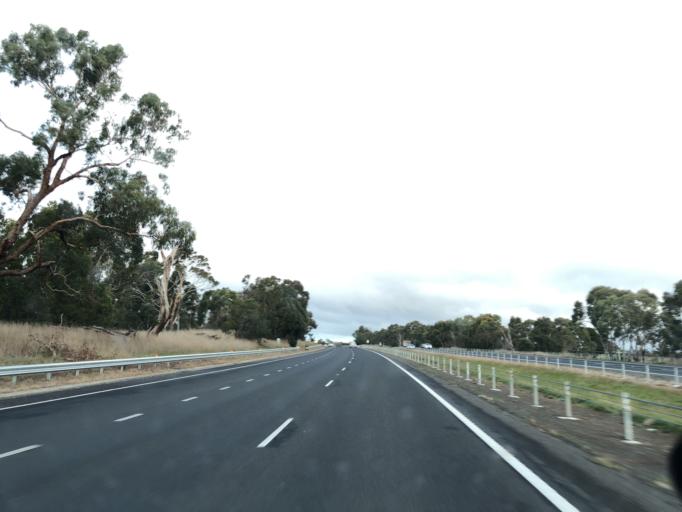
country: AU
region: Victoria
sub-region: Mount Alexander
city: Castlemaine
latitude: -37.2621
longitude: 144.4724
